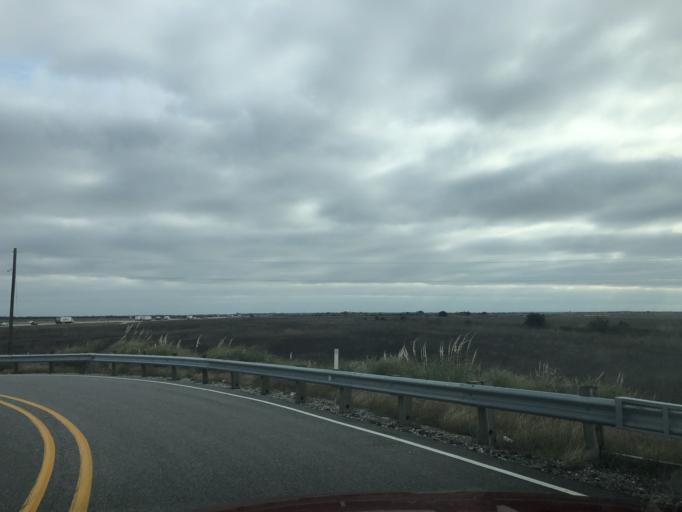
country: US
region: Texas
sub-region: Chambers County
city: Winnie
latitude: 29.8287
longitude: -94.4825
